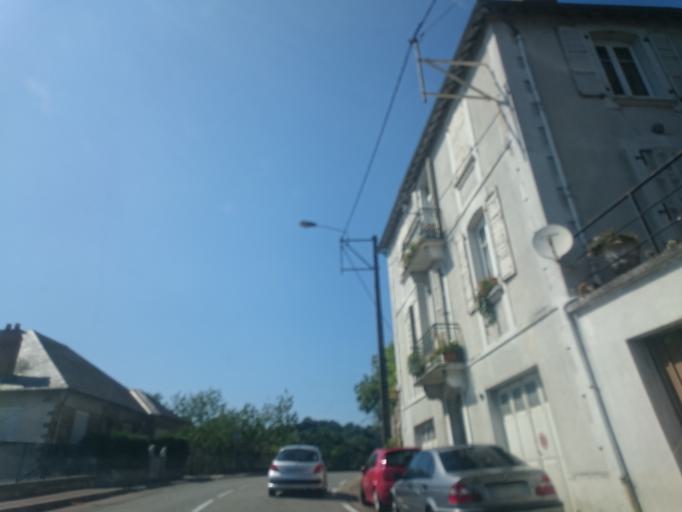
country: FR
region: Limousin
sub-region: Departement de la Correze
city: Tulle
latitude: 45.2745
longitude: 1.7719
